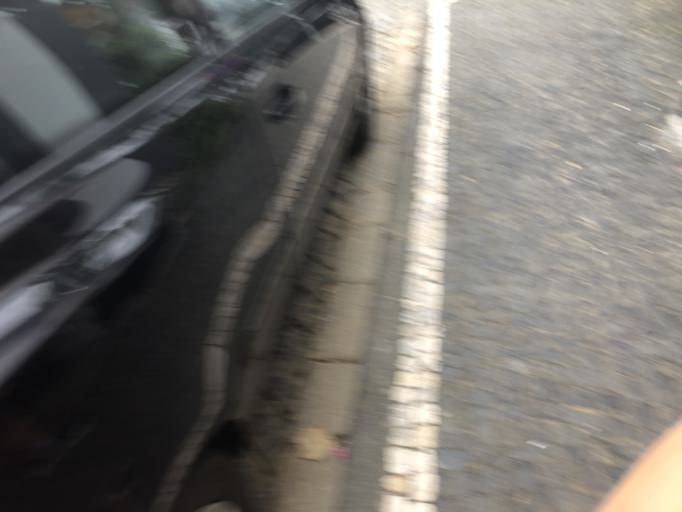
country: PT
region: Azores
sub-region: Angra do Heroismo
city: Angra do Heroismo
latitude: 38.6565
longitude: -27.2192
